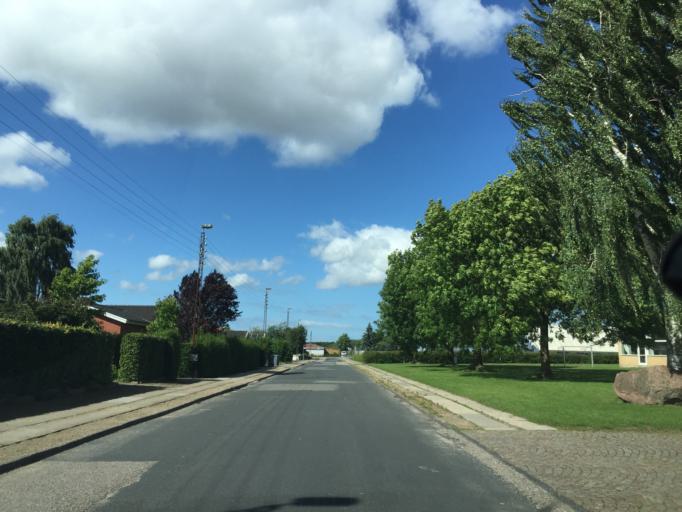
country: DK
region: South Denmark
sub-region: Odense Kommune
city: Odense
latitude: 55.3609
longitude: 10.3987
